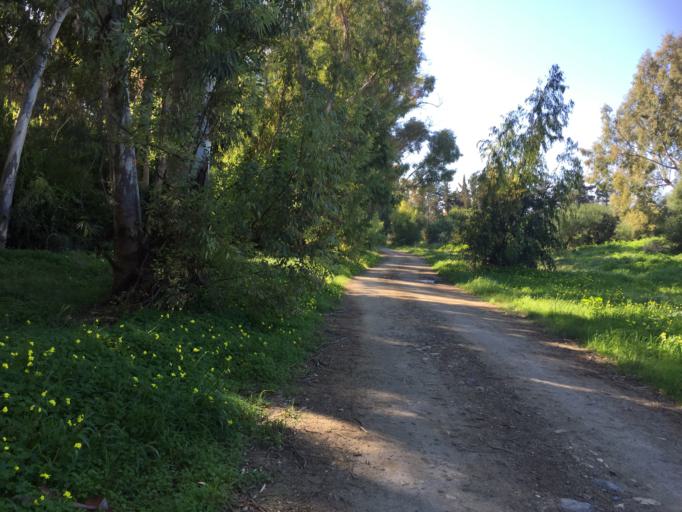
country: CY
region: Larnaka
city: Kolossi
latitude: 34.6294
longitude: 32.9593
